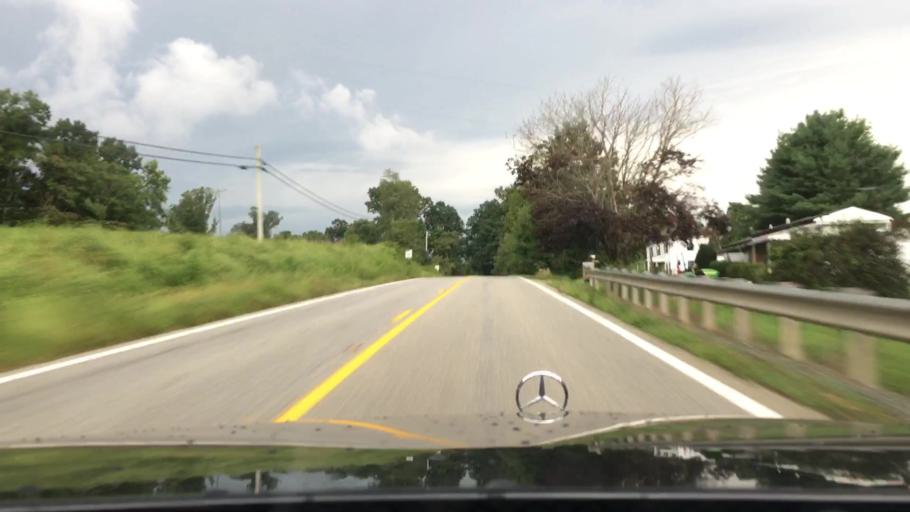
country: US
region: Virginia
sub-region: Nelson County
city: Lovingston
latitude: 37.7779
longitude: -78.9806
